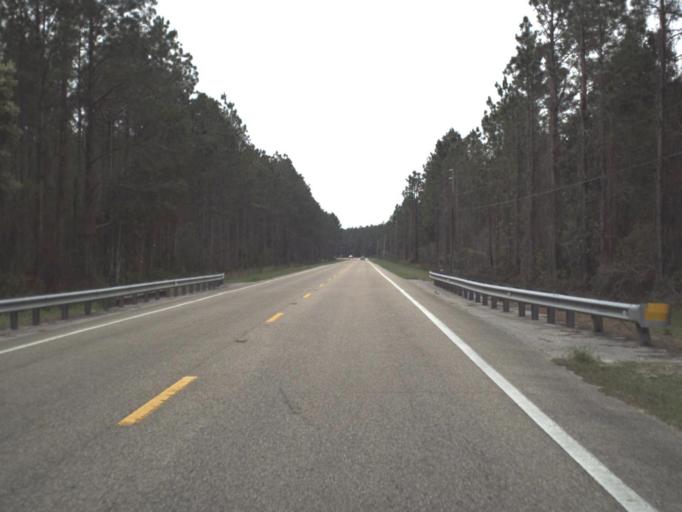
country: US
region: Florida
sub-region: Gulf County
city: Port Saint Joe
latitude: 29.8409
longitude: -85.2690
